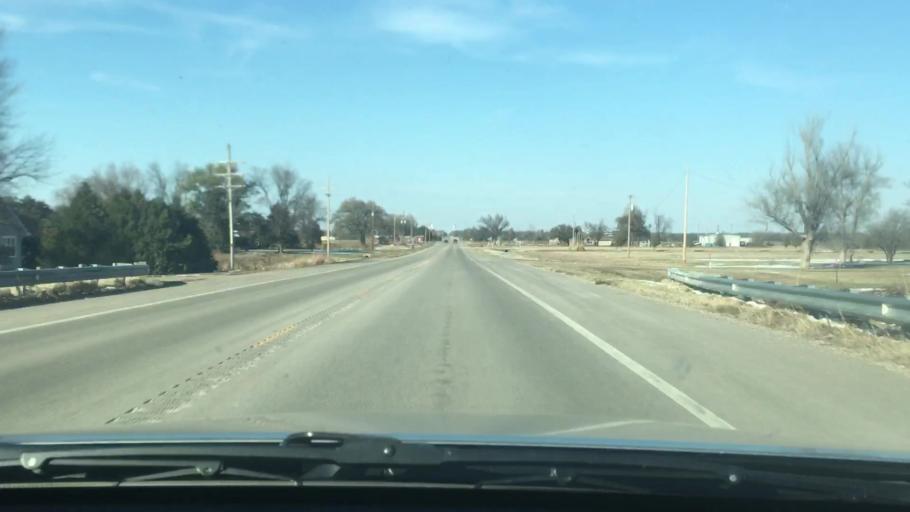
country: US
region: Kansas
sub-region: Rice County
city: Lyons
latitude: 38.3151
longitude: -98.2018
